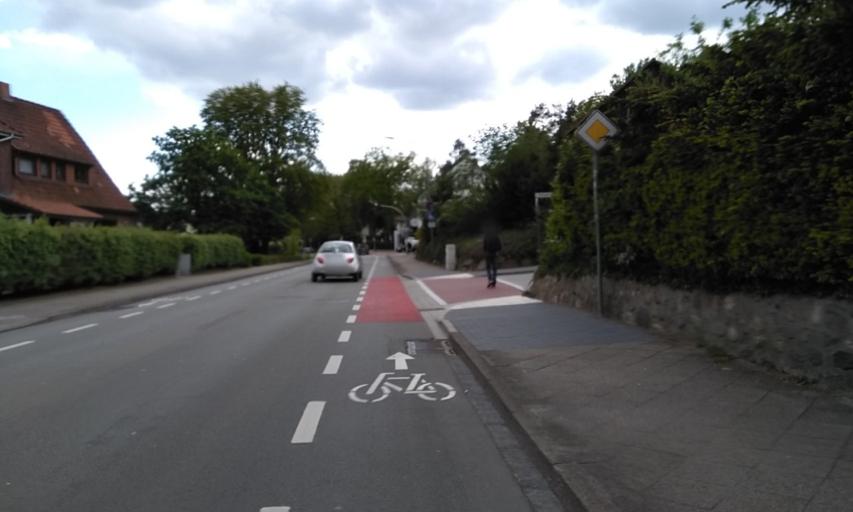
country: DE
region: Lower Saxony
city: Buxtehude
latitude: 53.4635
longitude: 9.6798
